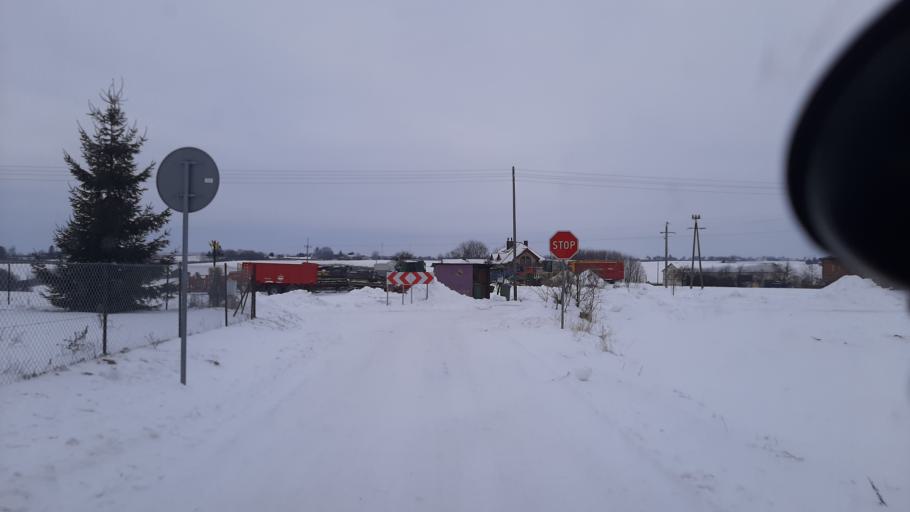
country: PL
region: Lublin Voivodeship
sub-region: Powiat lubelski
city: Garbow
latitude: 51.3318
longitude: 22.2915
